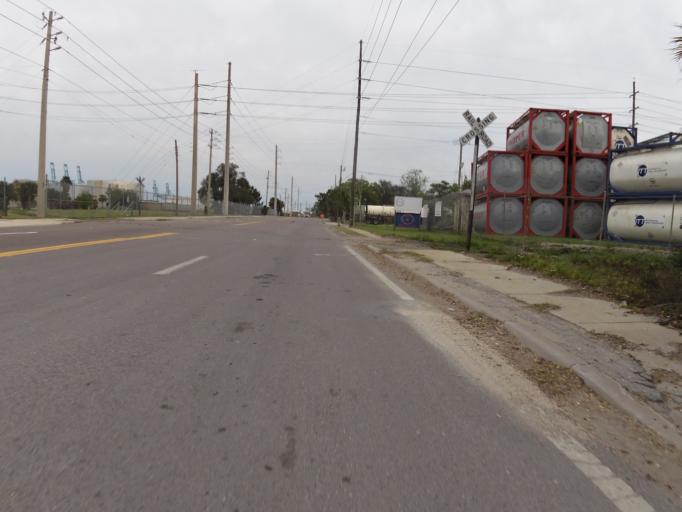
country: US
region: Florida
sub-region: Duval County
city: Jacksonville
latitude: 30.3633
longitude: -81.6278
